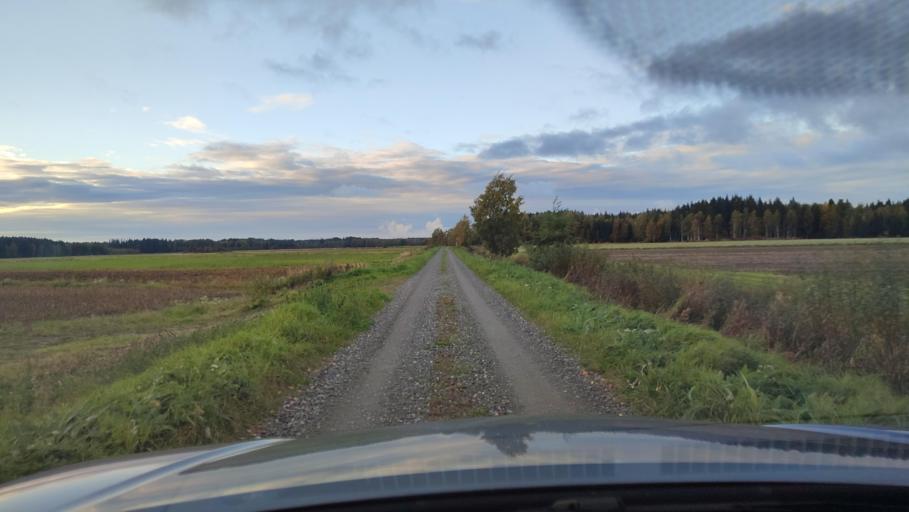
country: FI
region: Ostrobothnia
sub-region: Sydosterbotten
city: Kristinestad
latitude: 62.2408
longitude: 21.4547
